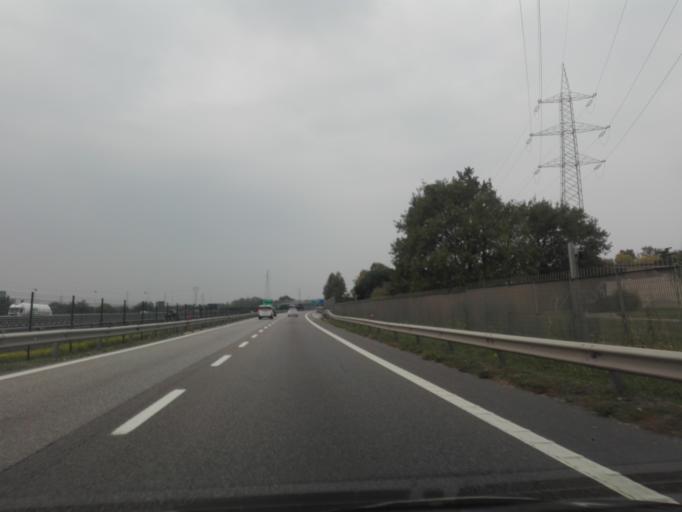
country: IT
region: Veneto
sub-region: Provincia di Verona
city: Verona
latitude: 45.3978
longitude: 10.9866
